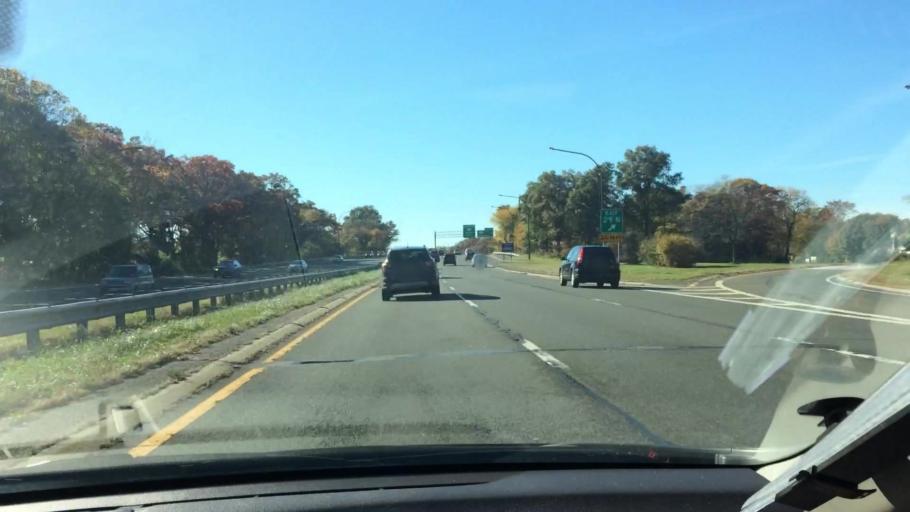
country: US
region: New York
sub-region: Nassau County
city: Plainedge
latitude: 40.7035
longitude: -73.4797
